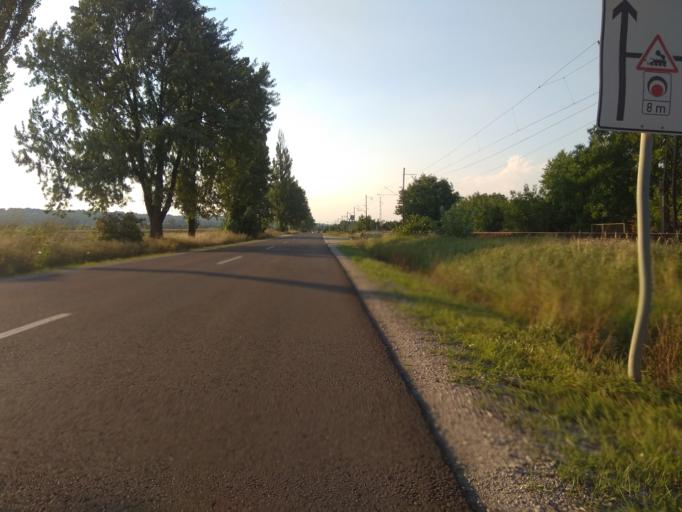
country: HU
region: Borsod-Abauj-Zemplen
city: Nyekladhaza
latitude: 47.9798
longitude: 20.8452
